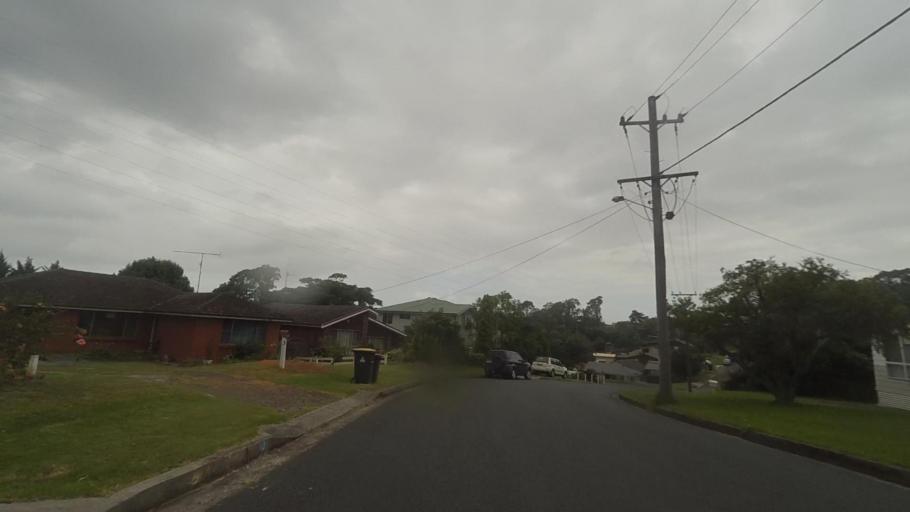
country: AU
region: New South Wales
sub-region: Wollongong
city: Cordeaux Heights
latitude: -34.4544
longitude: 150.8179
